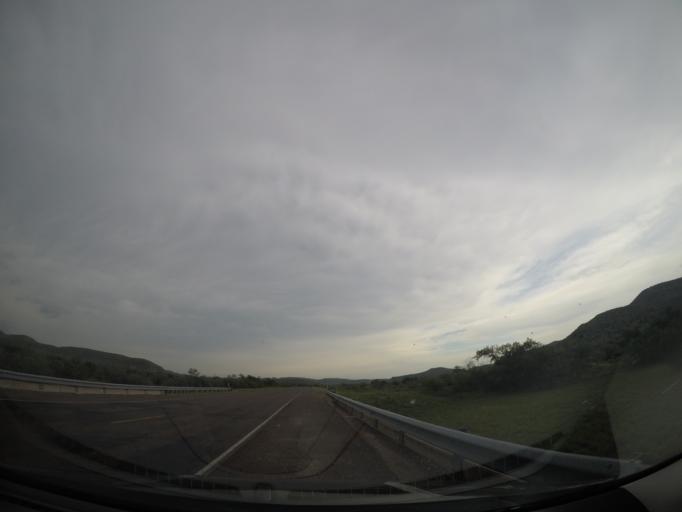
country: US
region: Texas
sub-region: Terrell County
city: Sanderson
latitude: 30.1627
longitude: -102.6580
